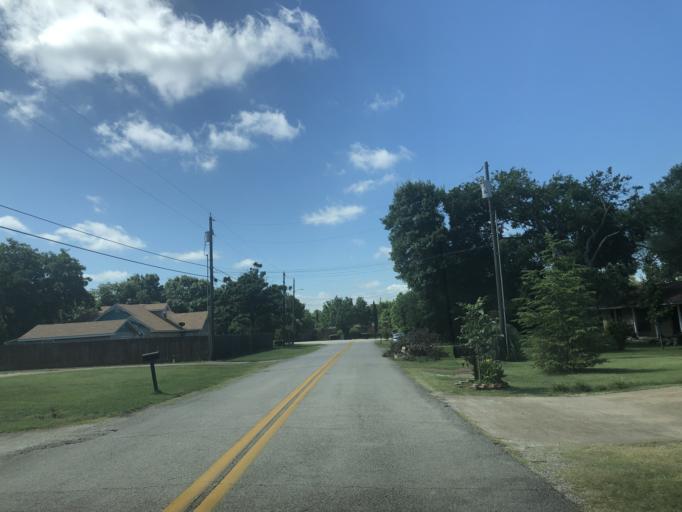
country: US
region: Texas
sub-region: Dallas County
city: Duncanville
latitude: 32.6491
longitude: -96.9355
